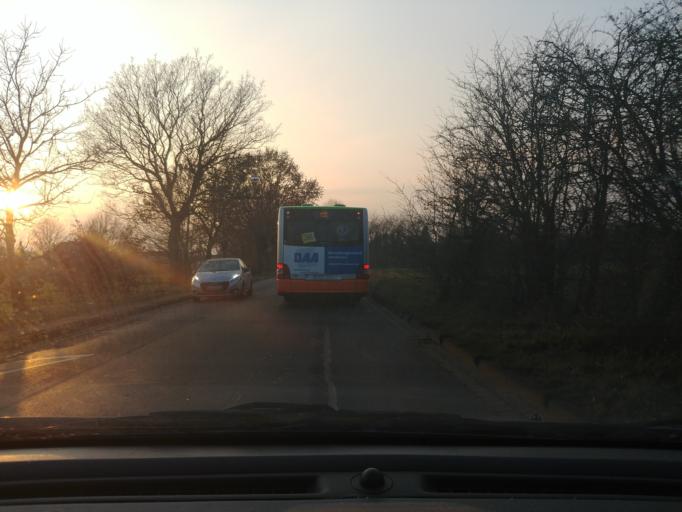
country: DE
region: Lower Saxony
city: Langenhagen
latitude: 52.4336
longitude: 9.6943
